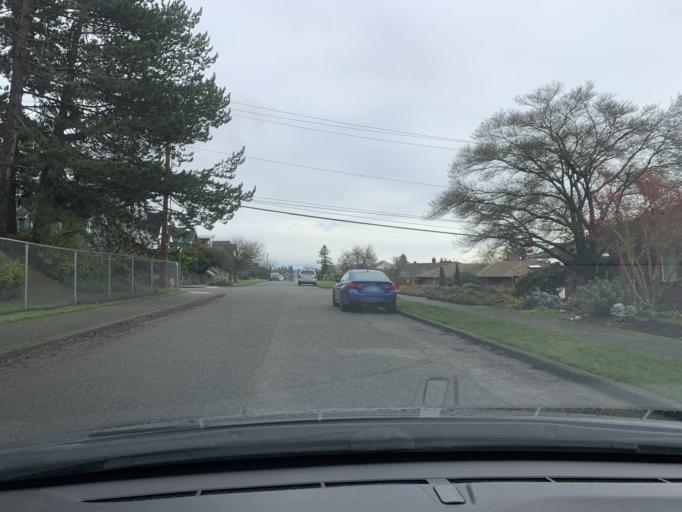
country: US
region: Washington
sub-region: King County
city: White Center
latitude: 47.5578
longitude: -122.3789
